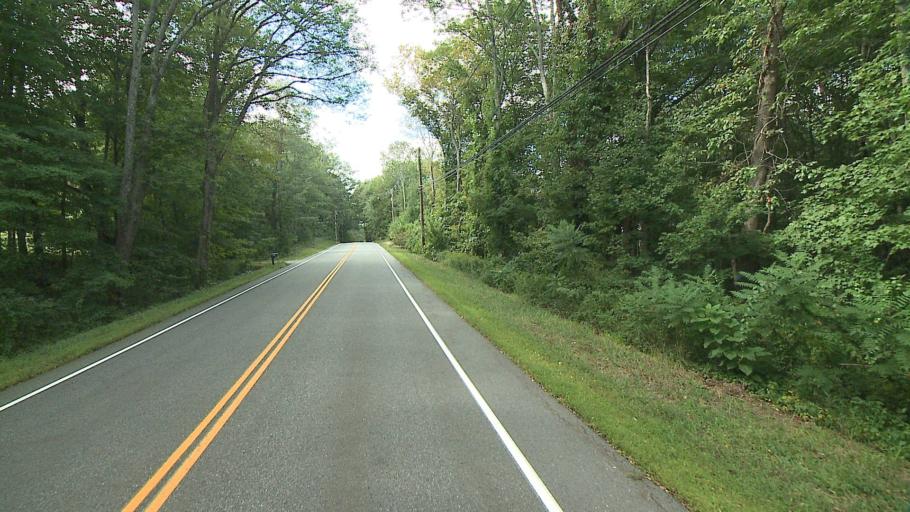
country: US
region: Connecticut
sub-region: Tolland County
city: Storrs
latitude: 41.8454
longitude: -72.2083
